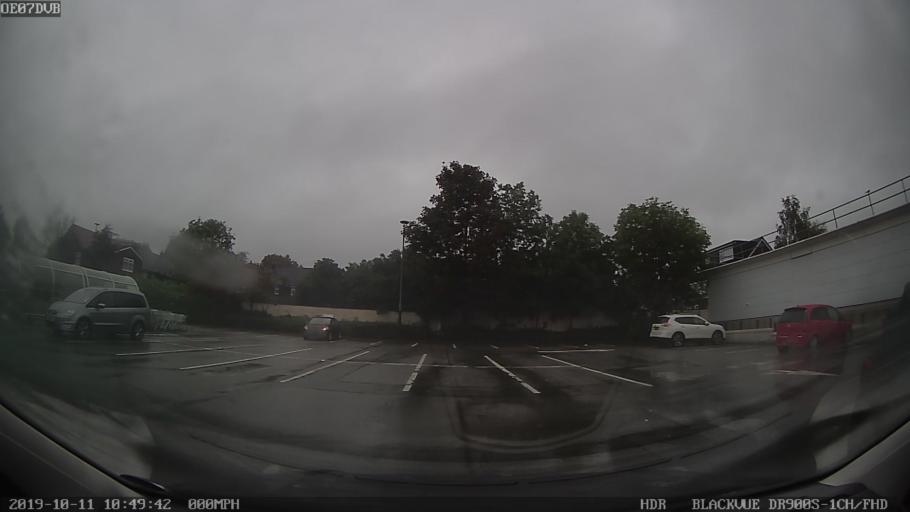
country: GB
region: England
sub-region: Borough of Oldham
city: Oldham
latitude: 53.5467
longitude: -2.1410
